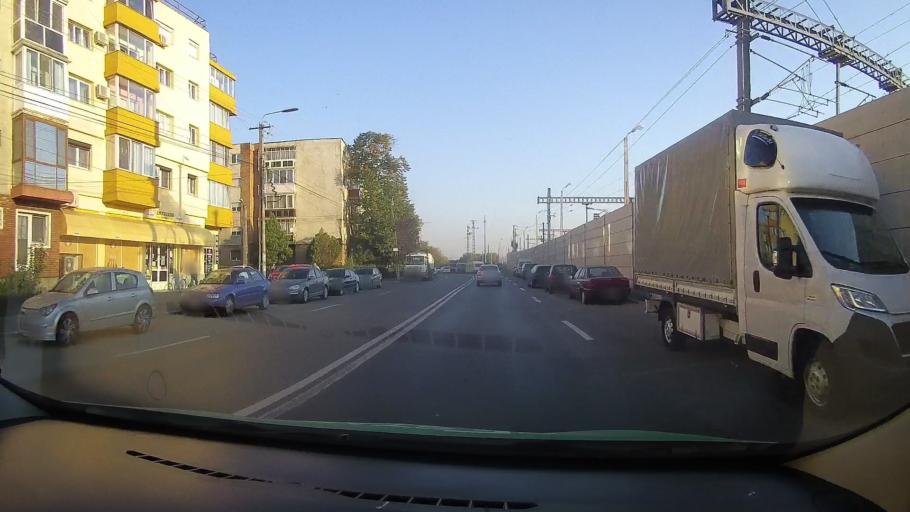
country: RO
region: Arad
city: Arad
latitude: 46.1980
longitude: 21.3204
